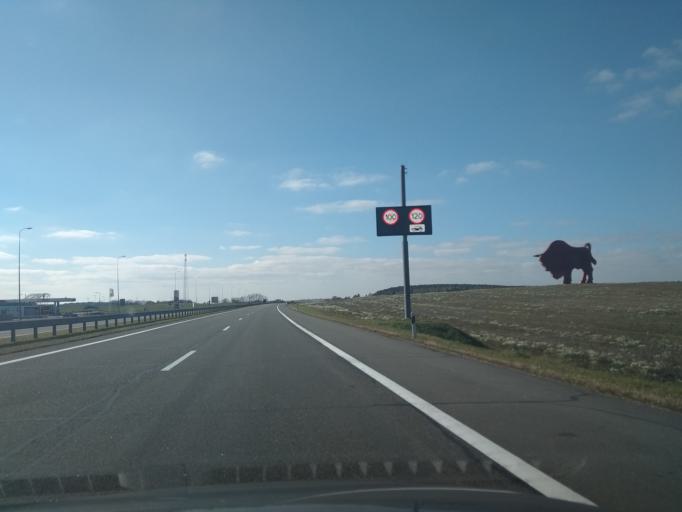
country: BY
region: Minsk
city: Snow
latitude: 53.2997
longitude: 26.3723
